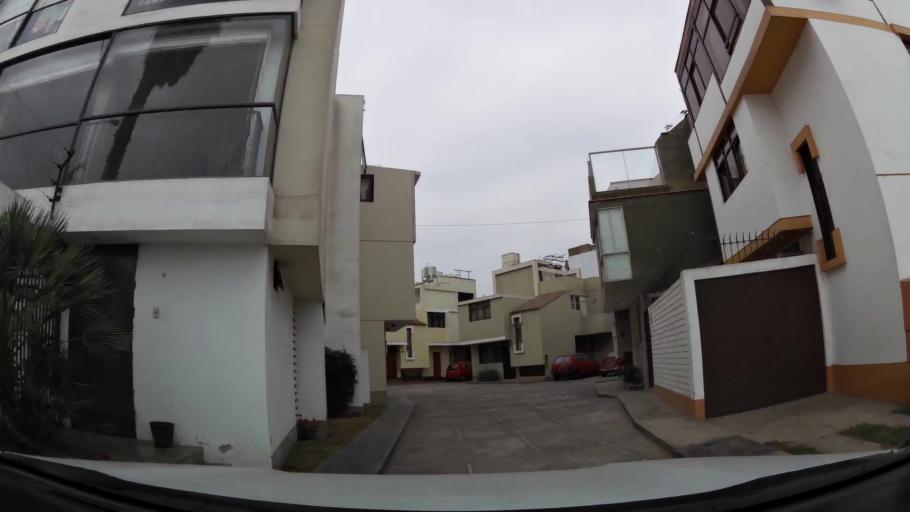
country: PE
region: Lima
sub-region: Lima
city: Surco
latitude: -12.1571
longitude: -77.0243
